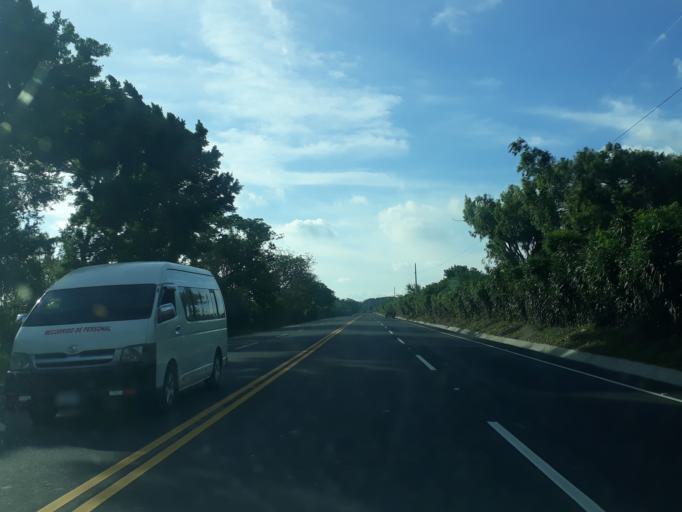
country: NI
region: Carazo
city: Diriamba
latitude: 11.9091
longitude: -86.2647
